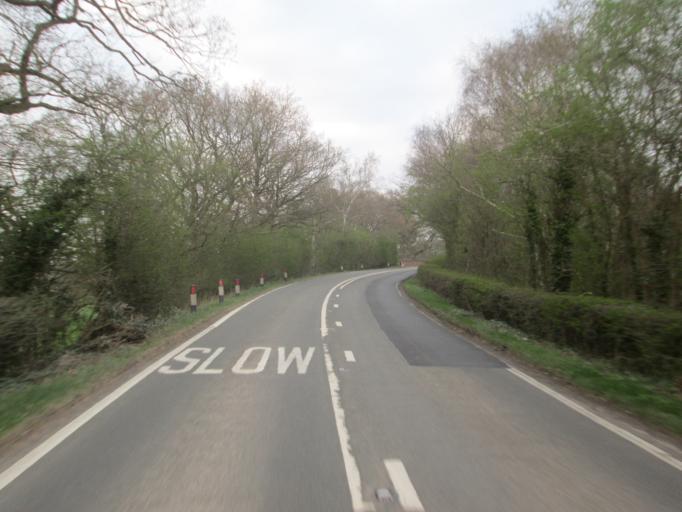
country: GB
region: England
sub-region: Derbyshire
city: Duffield
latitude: 53.0058
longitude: -1.5357
